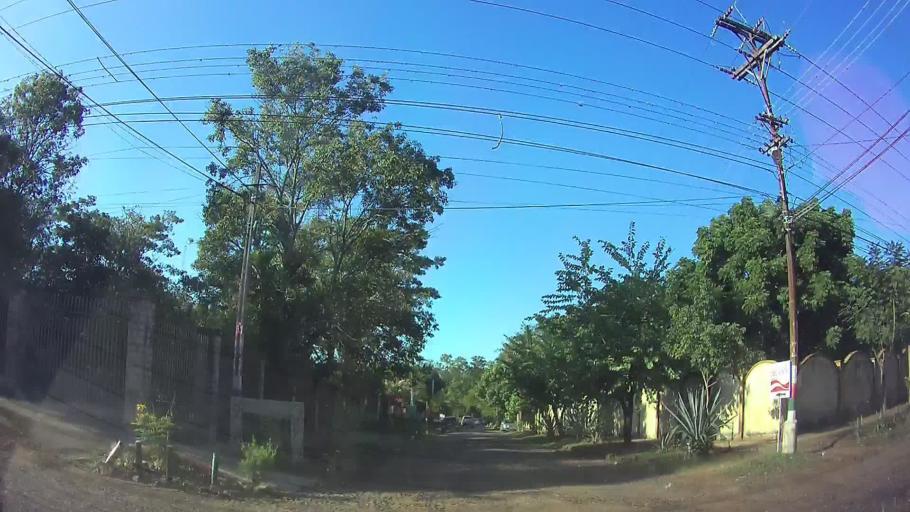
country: PY
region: Central
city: Aregua
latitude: -25.3112
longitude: -57.3818
